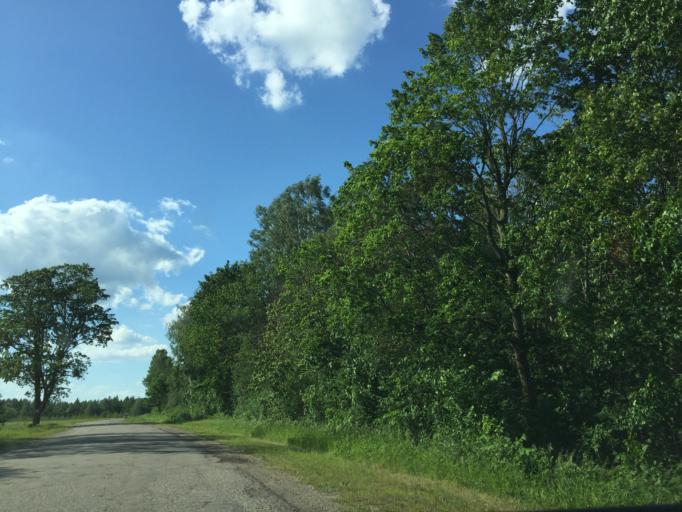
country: LV
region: Jaunpils
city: Jaunpils
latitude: 56.8834
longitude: 22.9879
